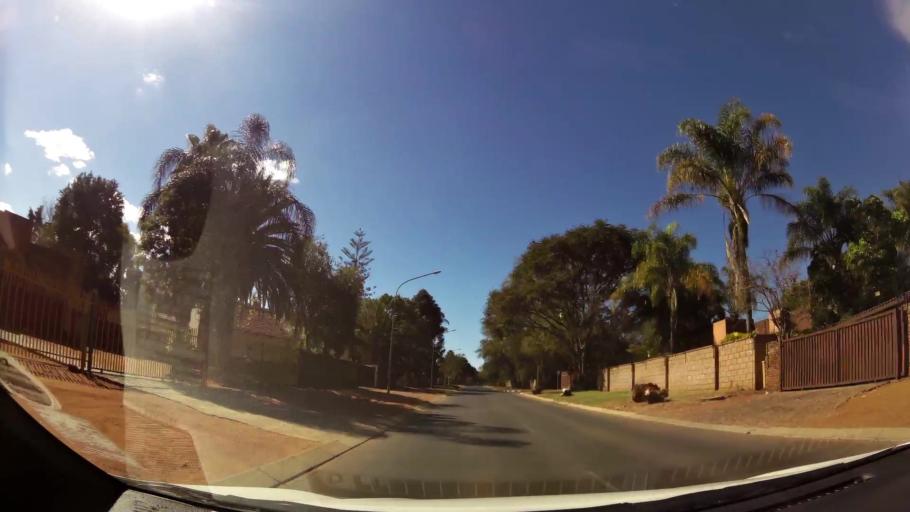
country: ZA
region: Limpopo
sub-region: Capricorn District Municipality
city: Polokwane
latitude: -23.9109
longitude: 29.4867
